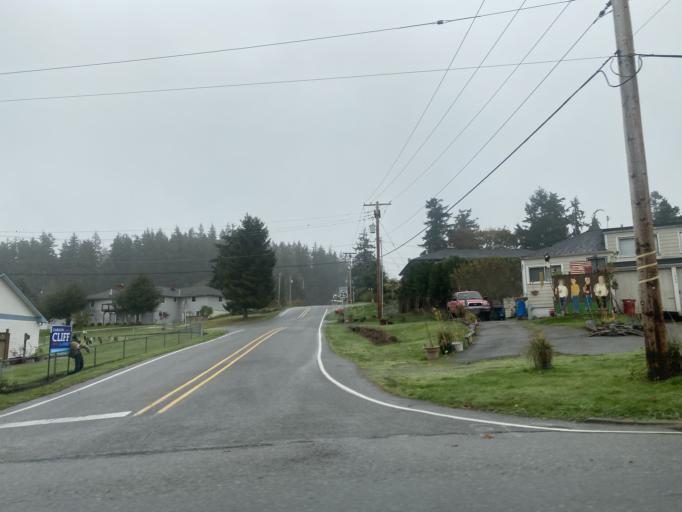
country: US
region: Washington
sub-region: Island County
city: Freeland
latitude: 48.0115
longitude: -122.5272
